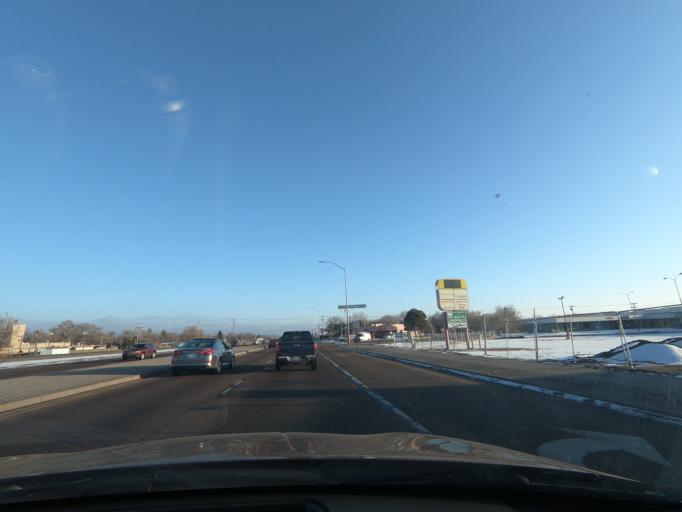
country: US
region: Colorado
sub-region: El Paso County
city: Security-Widefield
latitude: 38.7504
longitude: -104.7436
